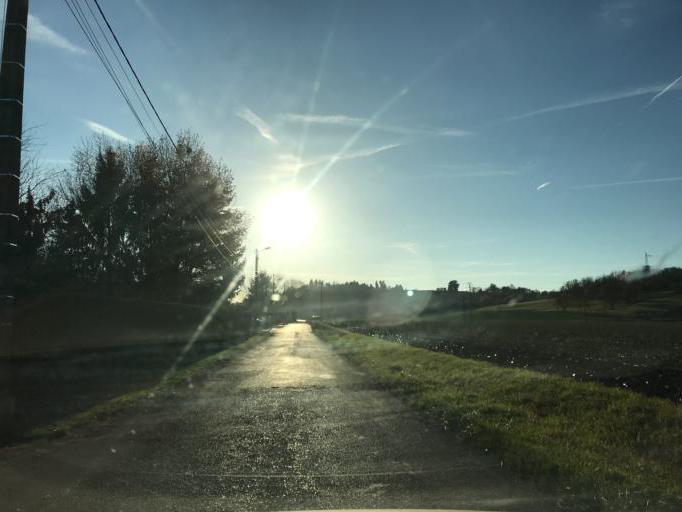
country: FR
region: Rhone-Alpes
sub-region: Departement de l'Ain
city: Meximieux
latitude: 45.9177
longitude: 5.2158
